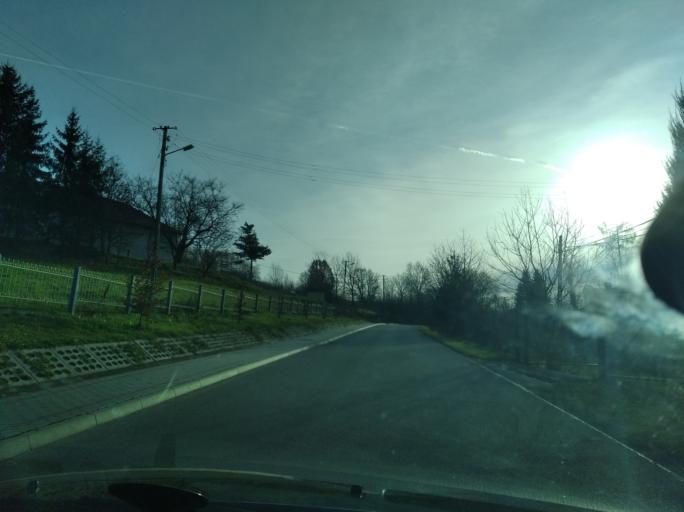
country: PL
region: Subcarpathian Voivodeship
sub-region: Powiat rzeszowski
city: Lubenia
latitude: 49.9307
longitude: 21.9252
